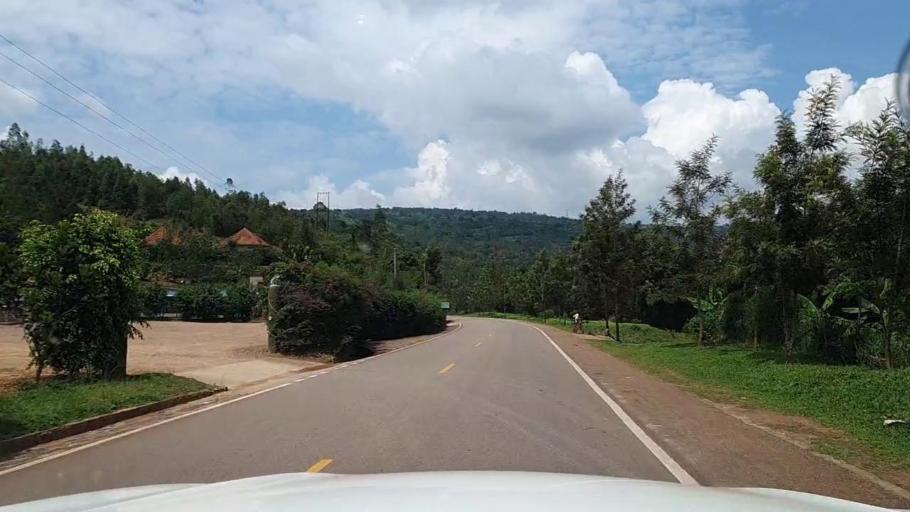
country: RW
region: Kigali
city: Kigali
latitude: -1.8431
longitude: 30.0899
